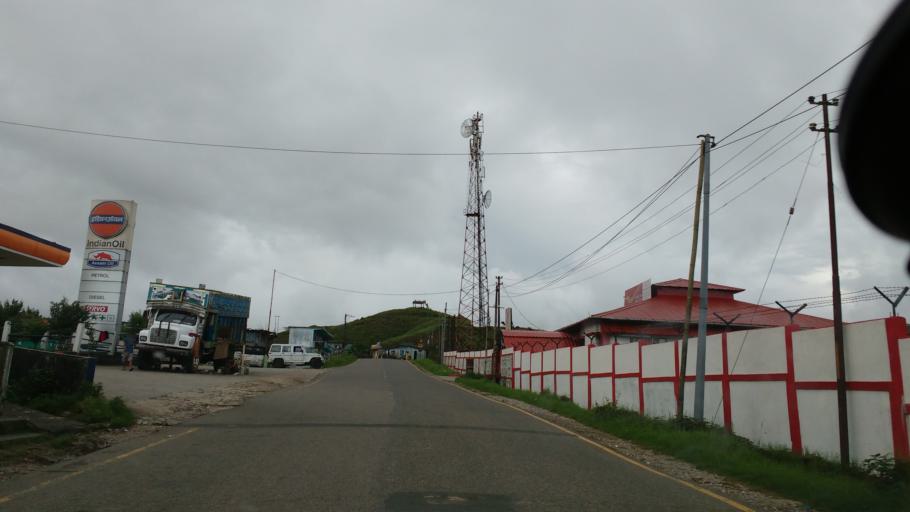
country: IN
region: Meghalaya
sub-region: East Khasi Hills
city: Cherrapunji
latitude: 25.2716
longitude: 91.7328
